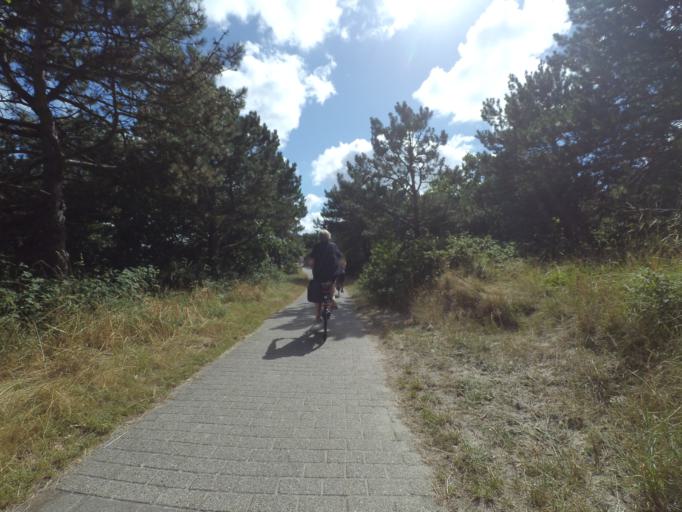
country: NL
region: North Holland
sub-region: Gemeente Texel
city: Den Burg
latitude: 53.1008
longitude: 4.7619
